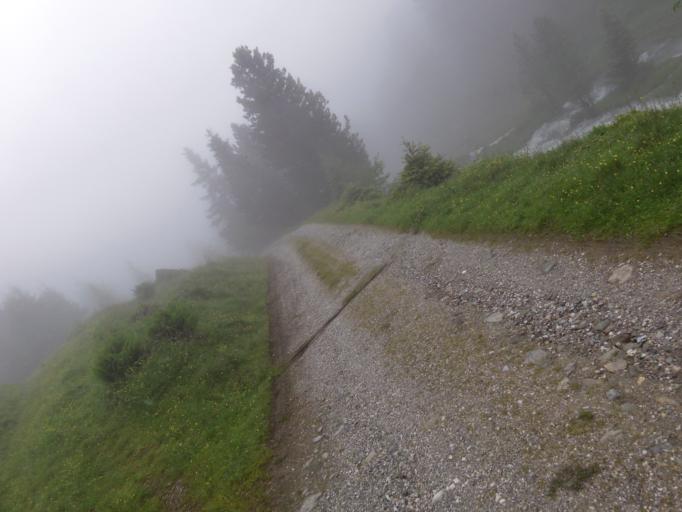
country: AT
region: Tyrol
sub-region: Politischer Bezirk Innsbruck Land
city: Neustift im Stubaital
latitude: 47.0551
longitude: 11.2181
